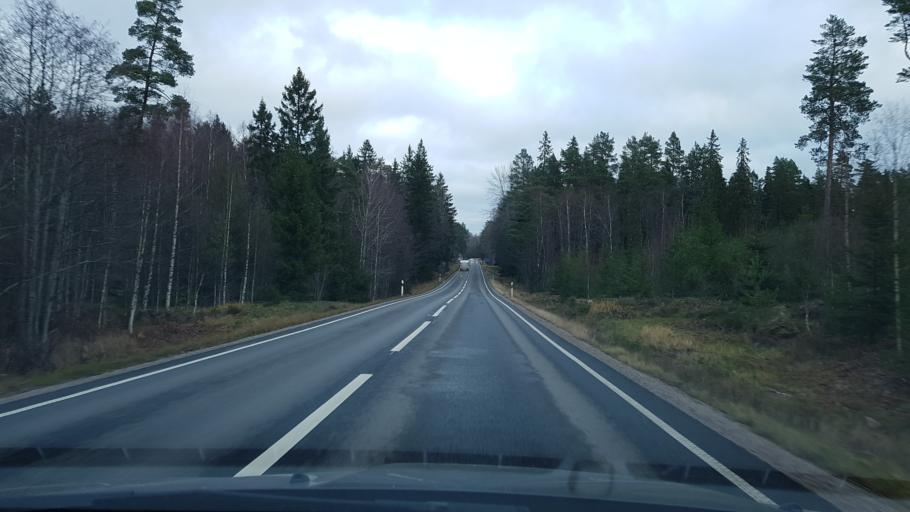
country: SE
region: Stockholm
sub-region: Norrtalje Kommun
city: Skanninge
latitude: 60.0252
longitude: 18.4114
